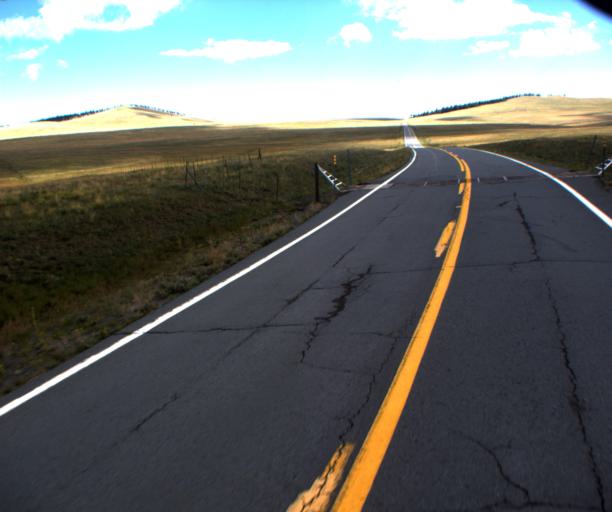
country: US
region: Arizona
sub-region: Apache County
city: Eagar
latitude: 33.9633
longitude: -109.3874
